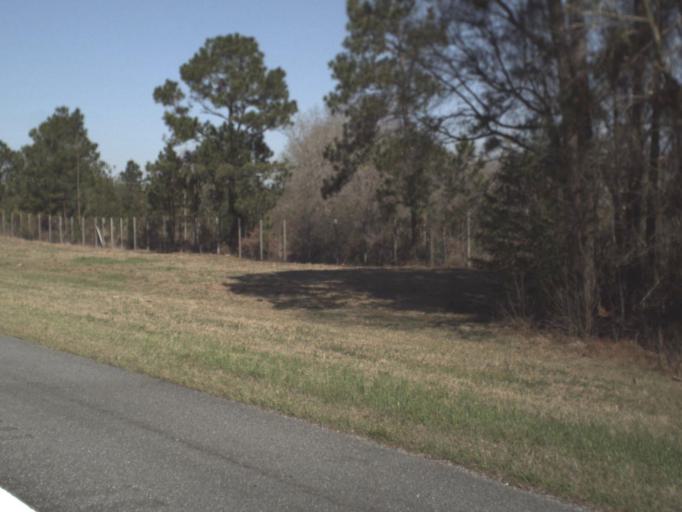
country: US
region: Florida
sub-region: Jackson County
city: Marianna
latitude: 30.7019
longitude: -85.1375
